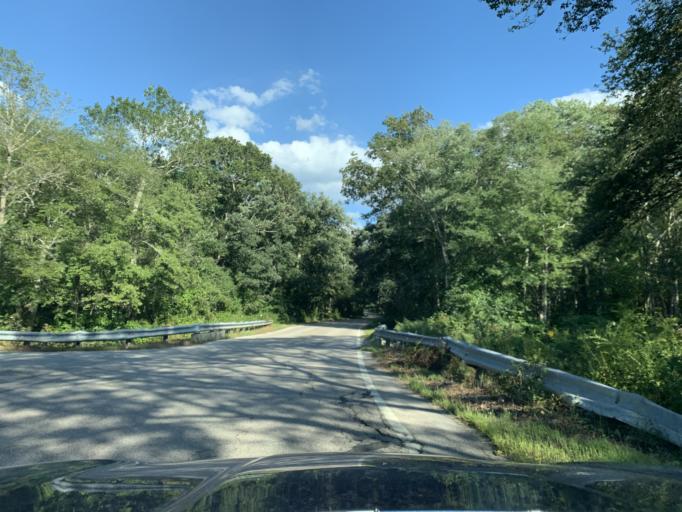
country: US
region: Rhode Island
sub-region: Washington County
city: Charlestown
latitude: 41.4641
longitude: -71.6284
